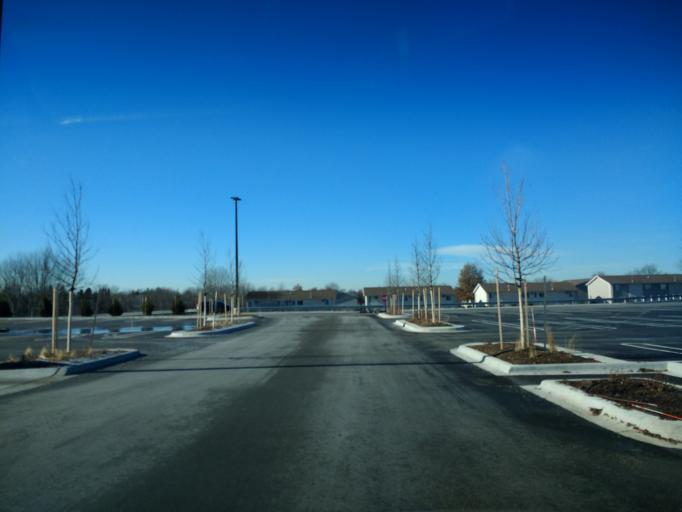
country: US
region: Iowa
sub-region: Scott County
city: Bettendorf
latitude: 41.5756
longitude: -90.5339
